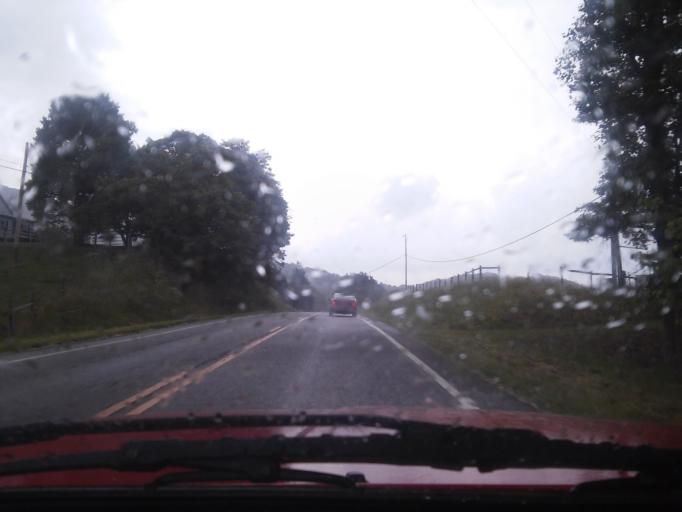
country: US
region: Virginia
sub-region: Montgomery County
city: Blacksburg
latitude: 37.3235
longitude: -80.4542
